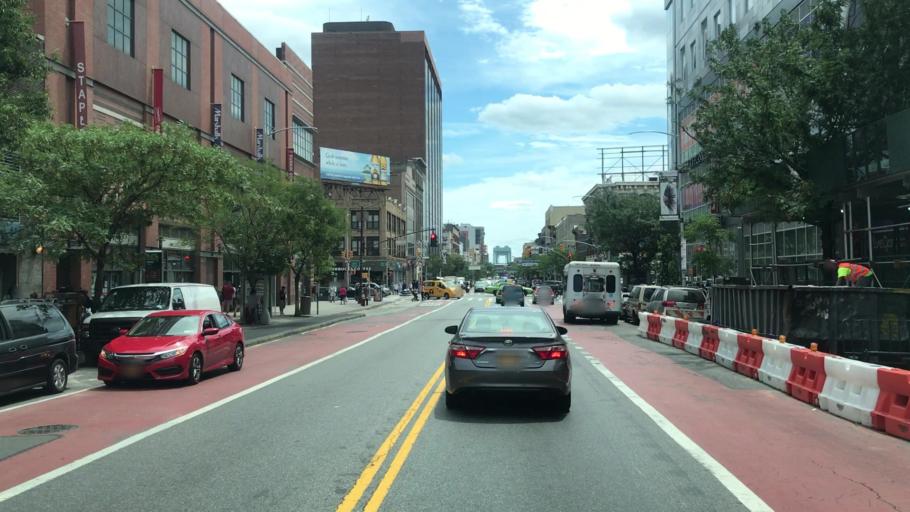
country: US
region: New York
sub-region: New York County
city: Manhattan
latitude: 40.8082
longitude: -73.9464
